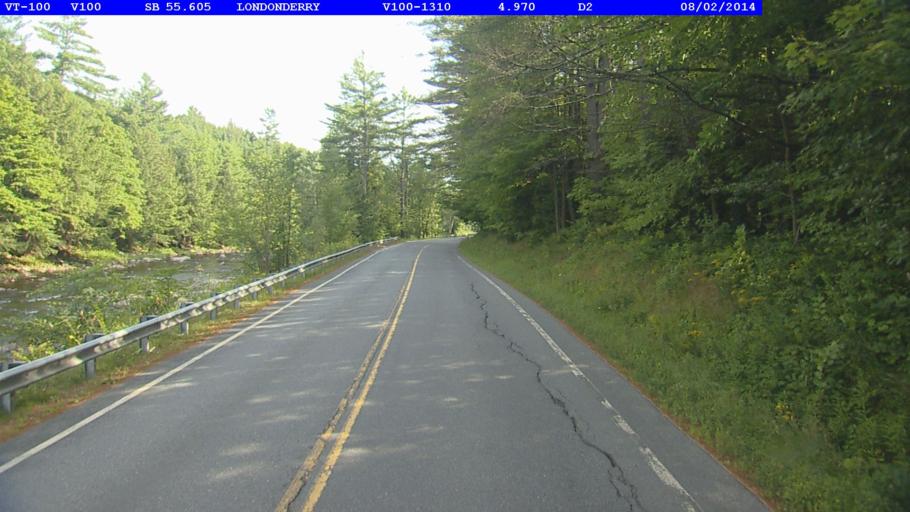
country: US
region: Vermont
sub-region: Windsor County
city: Chester
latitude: 43.2187
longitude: -72.8222
